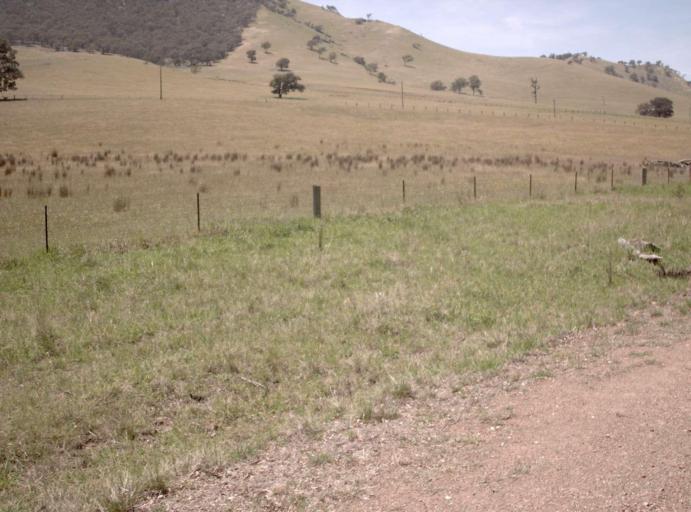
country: AU
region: Victoria
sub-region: East Gippsland
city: Bairnsdale
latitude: -37.3352
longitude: 147.7855
